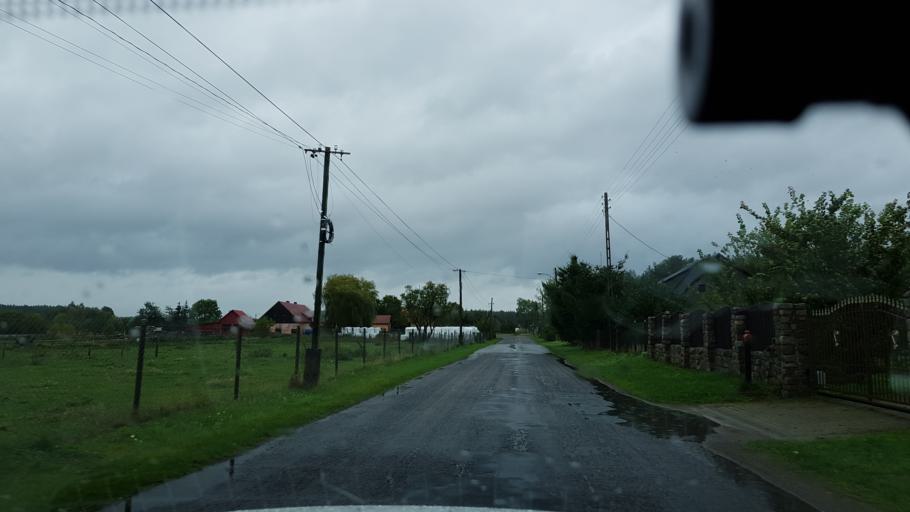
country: PL
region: West Pomeranian Voivodeship
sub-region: Powiat goleniowski
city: Przybiernow
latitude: 53.7578
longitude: 14.7009
